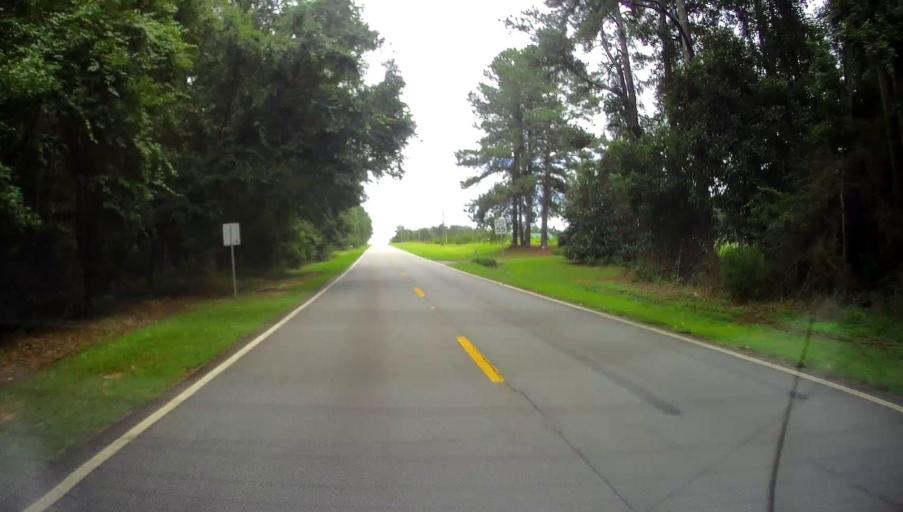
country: US
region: Georgia
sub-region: Twiggs County
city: Jeffersonville
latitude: 32.6796
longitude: -83.3208
